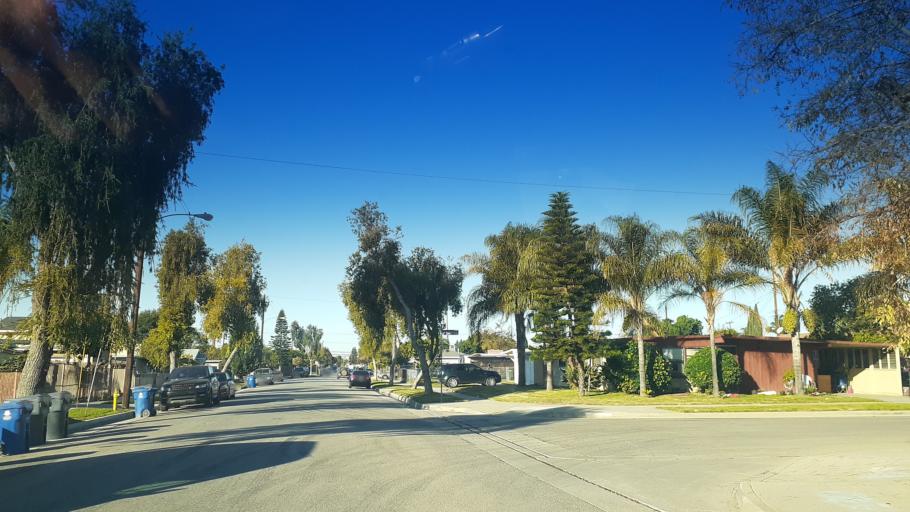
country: US
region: California
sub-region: Los Angeles County
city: Hawaiian Gardens
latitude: 33.8442
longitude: -118.0791
